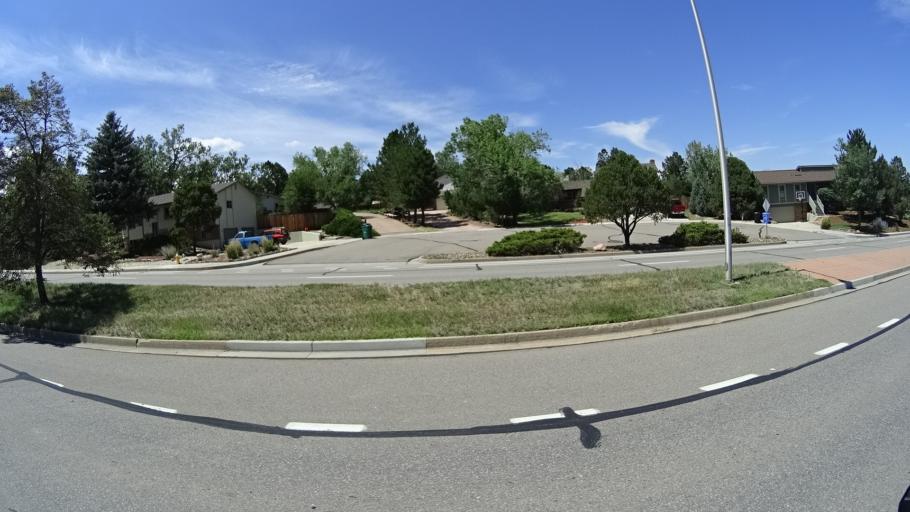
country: US
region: Colorado
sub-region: El Paso County
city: Air Force Academy
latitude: 38.9301
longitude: -104.8208
